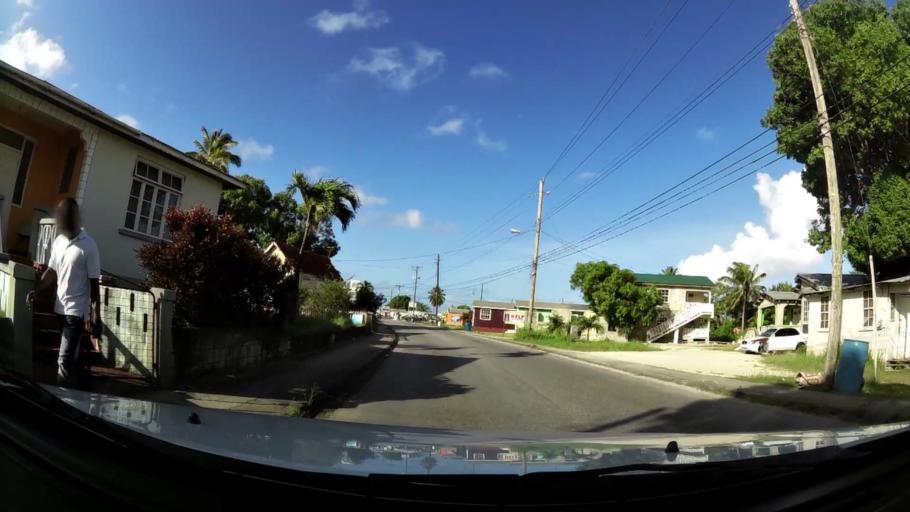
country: BB
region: Saint Michael
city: Bridgetown
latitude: 13.1088
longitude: -59.5943
